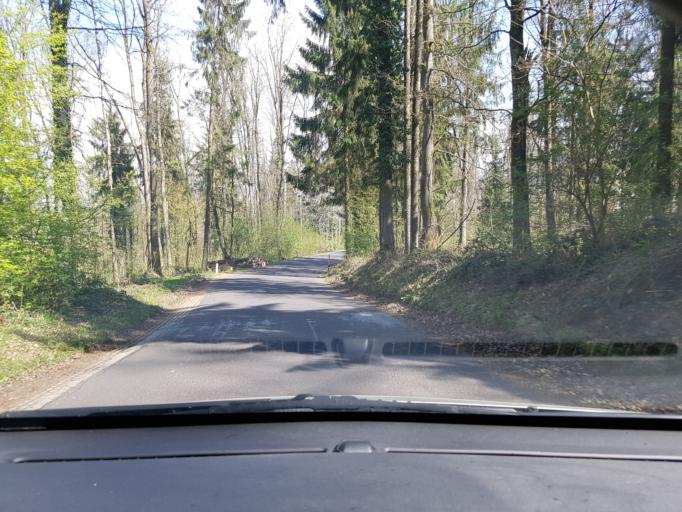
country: AT
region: Upper Austria
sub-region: Politischer Bezirk Linz-Land
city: Sankt Florian
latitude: 48.2065
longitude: 14.3511
